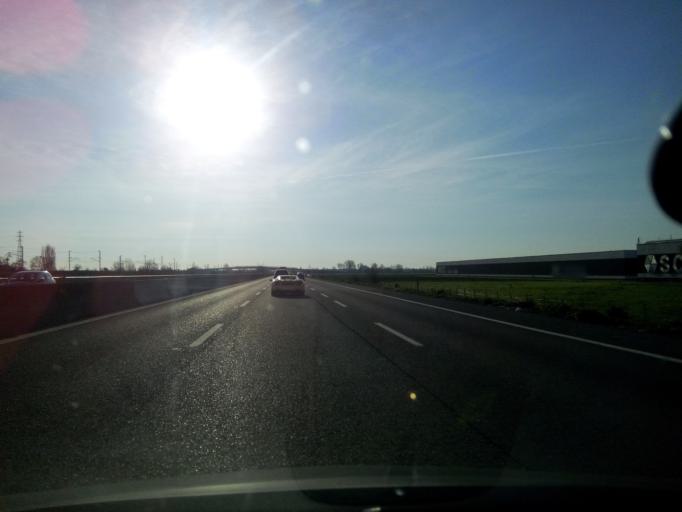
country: IT
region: Emilia-Romagna
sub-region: Provincia di Parma
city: Baganzola
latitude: 44.8584
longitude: 10.2616
